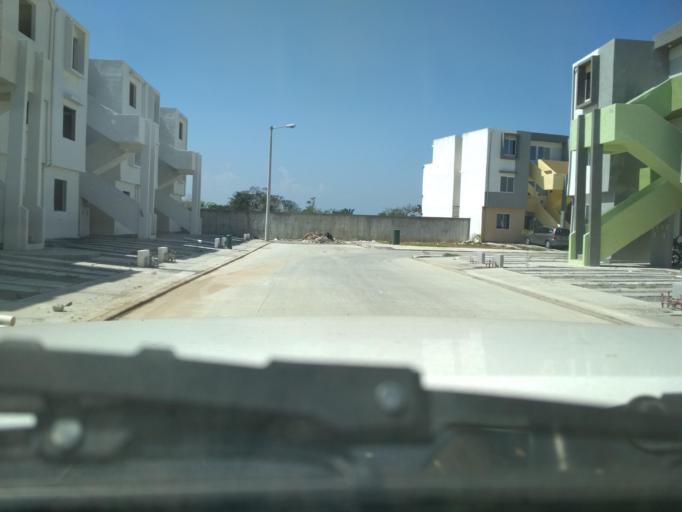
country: MX
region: Veracruz
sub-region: Medellin
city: Fraccionamiento Arboledas San Ramon
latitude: 19.0891
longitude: -96.1668
